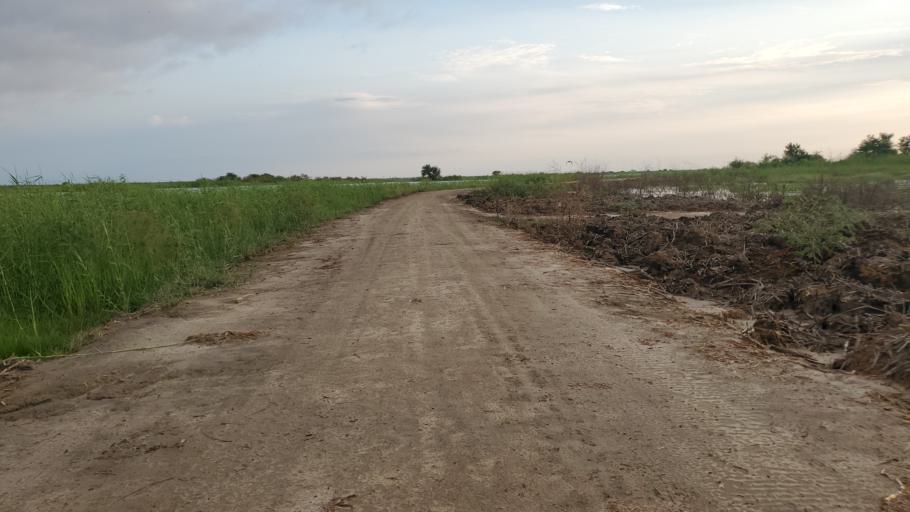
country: SN
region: Saint-Louis
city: Saint-Louis
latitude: 16.0092
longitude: -16.4014
